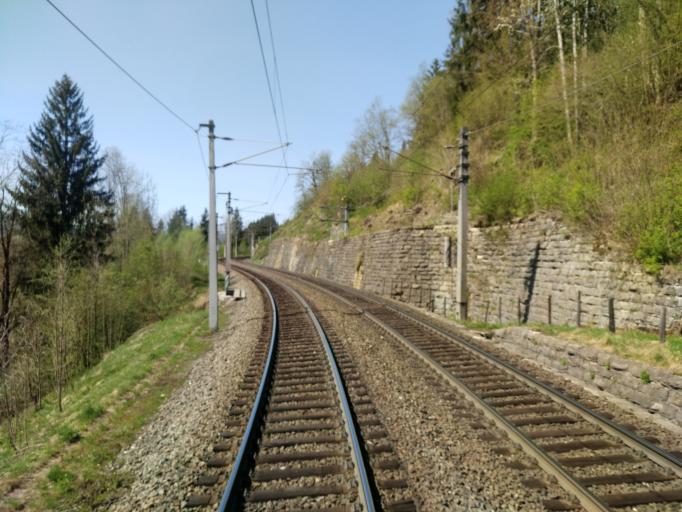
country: AT
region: Tyrol
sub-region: Politischer Bezirk Kitzbuhel
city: Hopfgarten im Brixental
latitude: 47.4318
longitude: 12.1827
